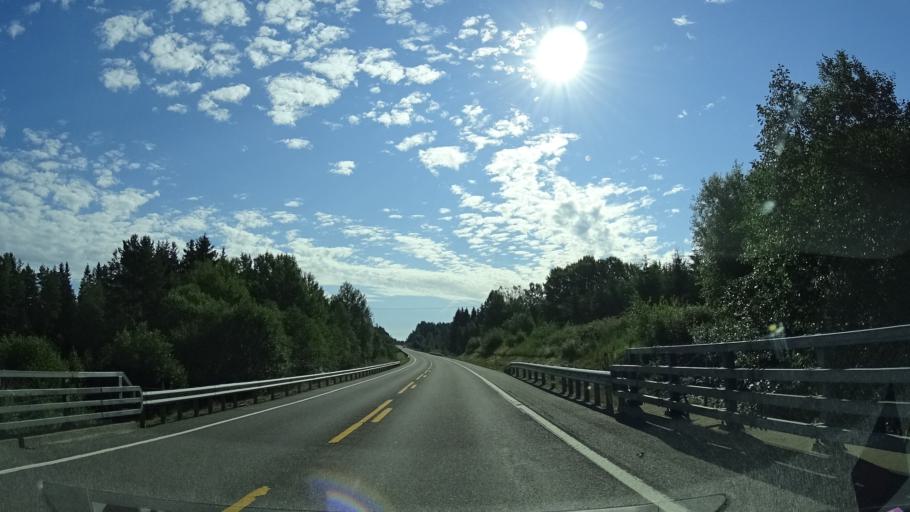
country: NO
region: Ostfold
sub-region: Marker
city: Orje
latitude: 59.5388
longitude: 11.5100
